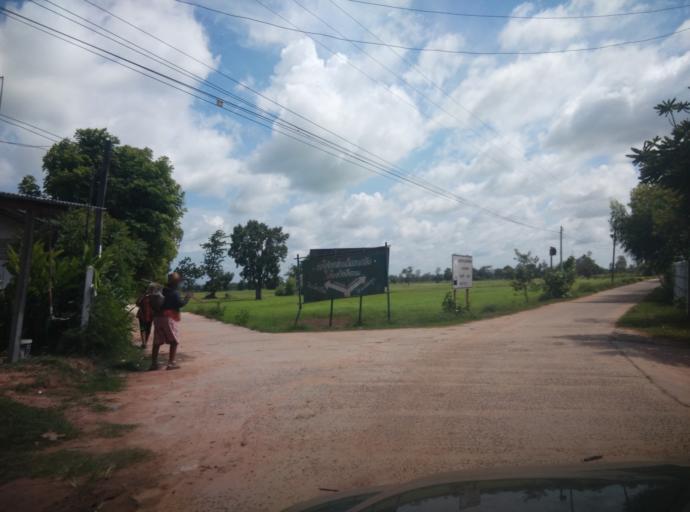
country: TH
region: Sisaket
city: Prang Ku
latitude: 14.9488
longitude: 104.0819
